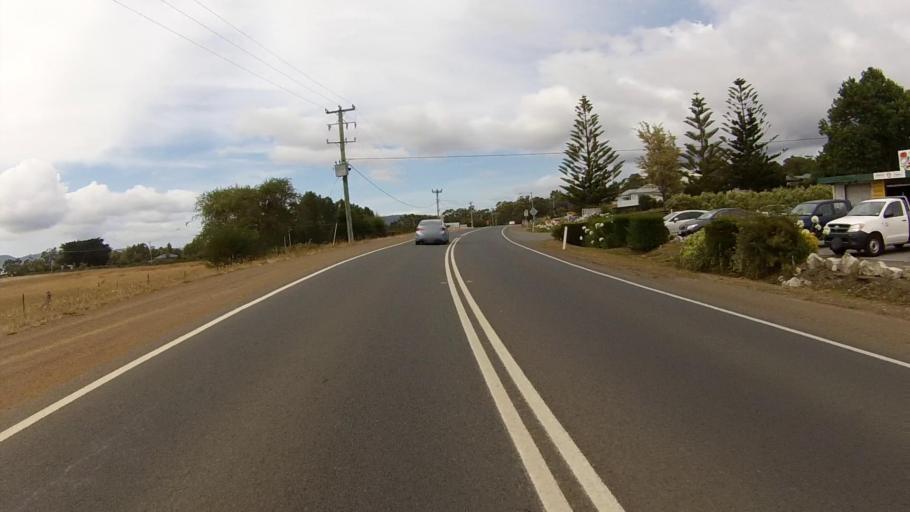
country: AU
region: Tasmania
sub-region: Kingborough
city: Margate
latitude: -43.0353
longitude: 147.2663
